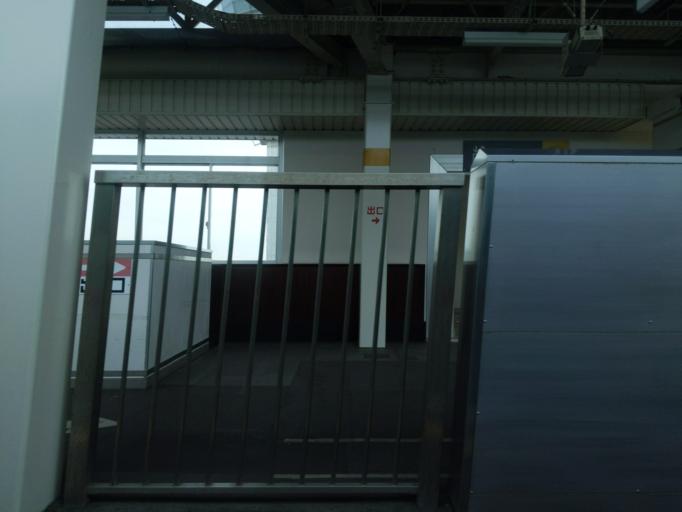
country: JP
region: Iwate
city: Ichinoseki
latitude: 38.7490
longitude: 141.0718
